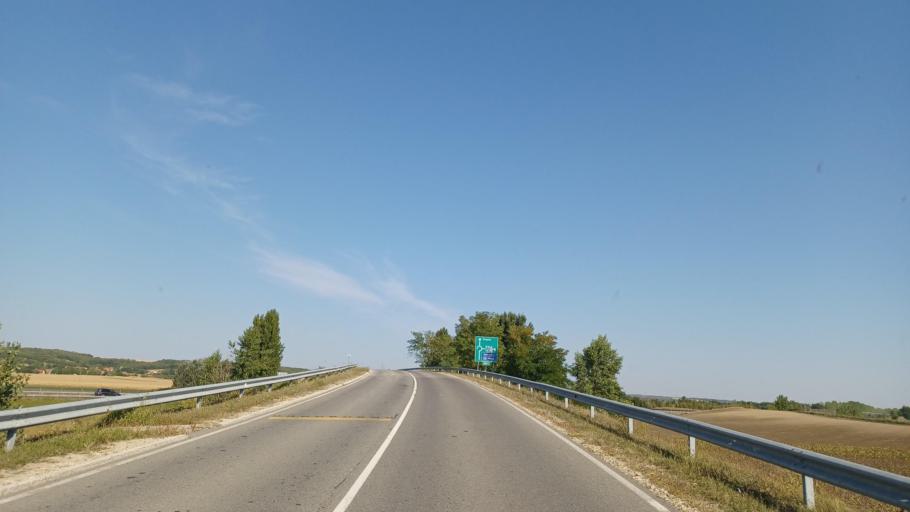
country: HU
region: Tolna
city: Dunaszentgyorgy
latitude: 46.5176
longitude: 18.7792
